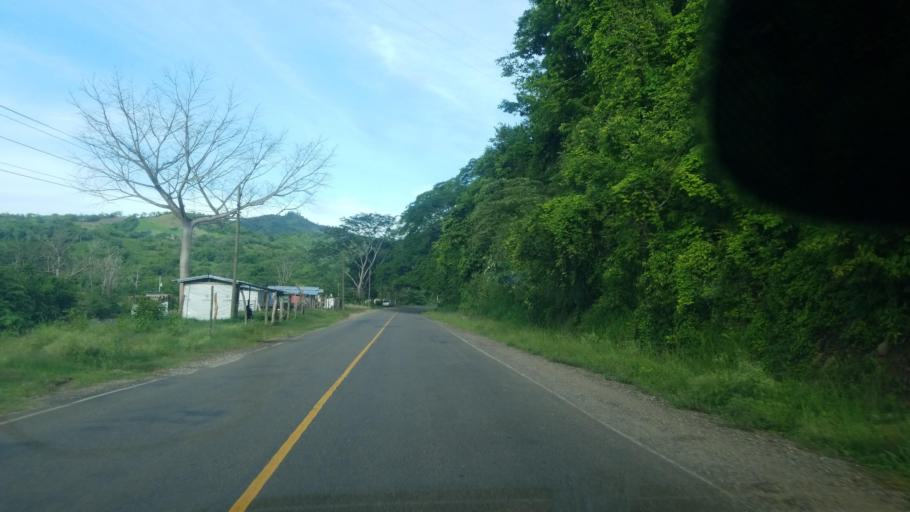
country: HN
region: Santa Barbara
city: Trinidad
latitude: 15.1217
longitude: -88.2034
